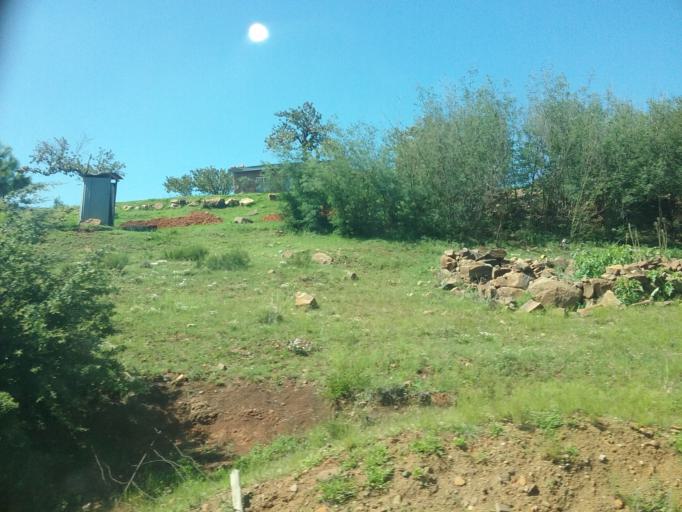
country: LS
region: Berea
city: Teyateyaneng
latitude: -29.2150
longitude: 27.8645
